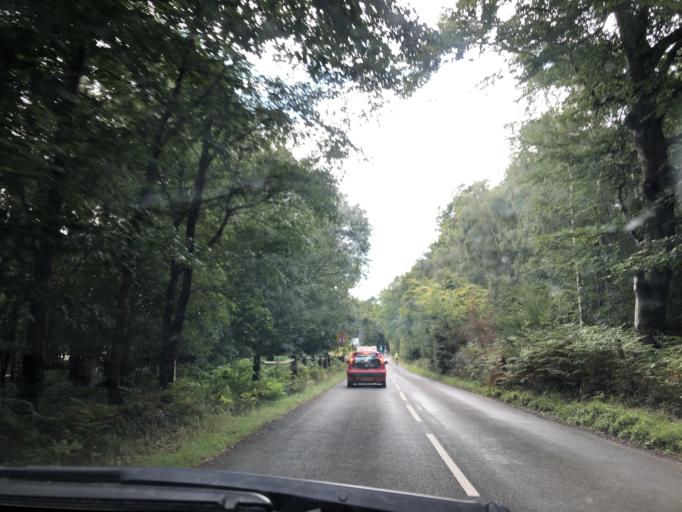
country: GB
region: England
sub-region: East Sussex
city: Forest Row
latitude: 51.0711
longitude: 0.0270
